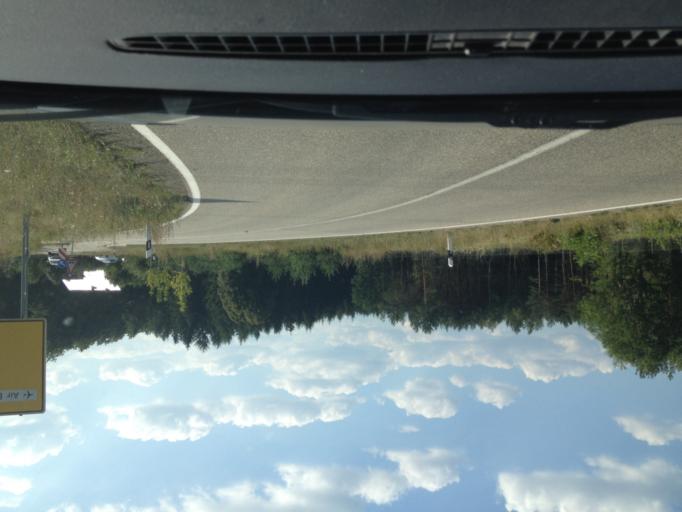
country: DE
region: Rheinland-Pfalz
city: Mackenbach
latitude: 49.4671
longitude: 7.5943
